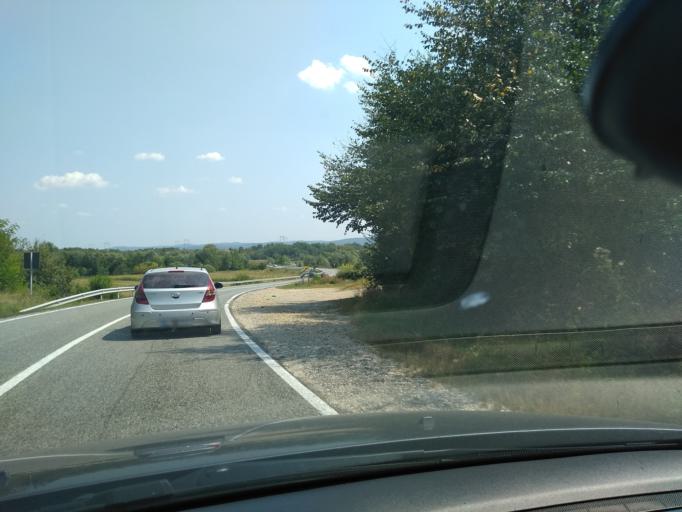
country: RO
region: Gorj
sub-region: Comuna Targu Carbunesti
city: Pojogeni
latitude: 45.0225
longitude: 23.5245
